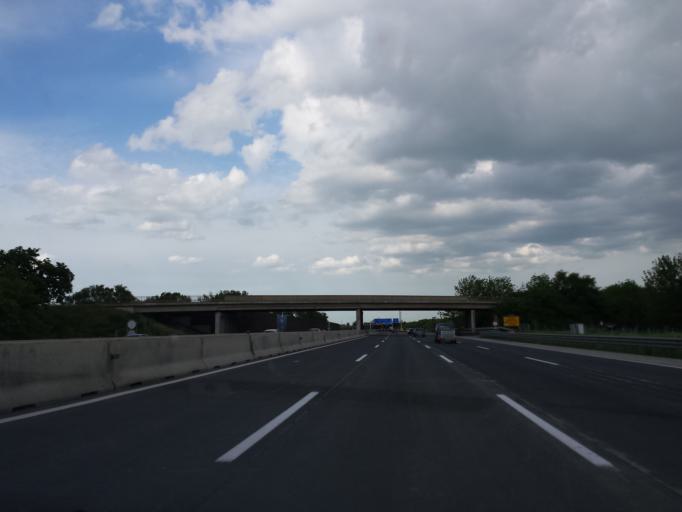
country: AT
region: Lower Austria
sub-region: Politischer Bezirk Baden
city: Pfaffstatten
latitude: 47.9820
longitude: 16.2657
